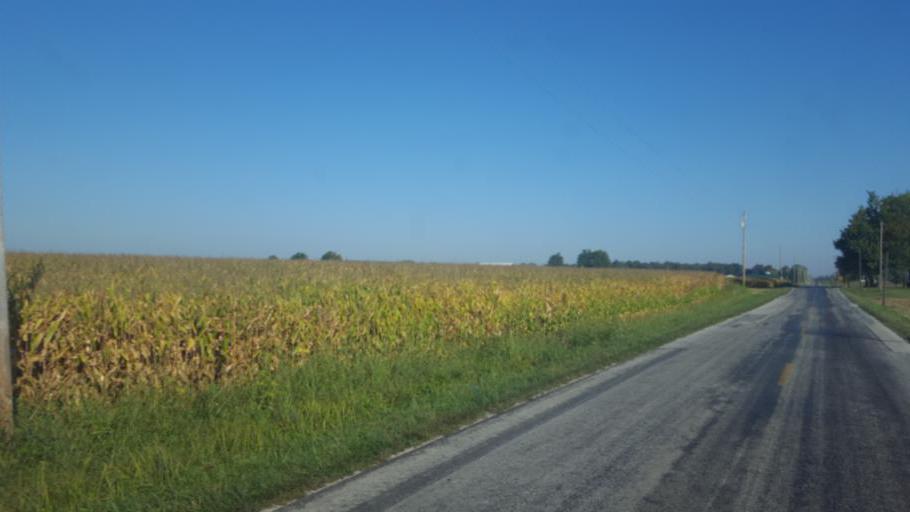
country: US
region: Ohio
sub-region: Union County
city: Richwood
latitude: 40.5433
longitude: -83.3889
